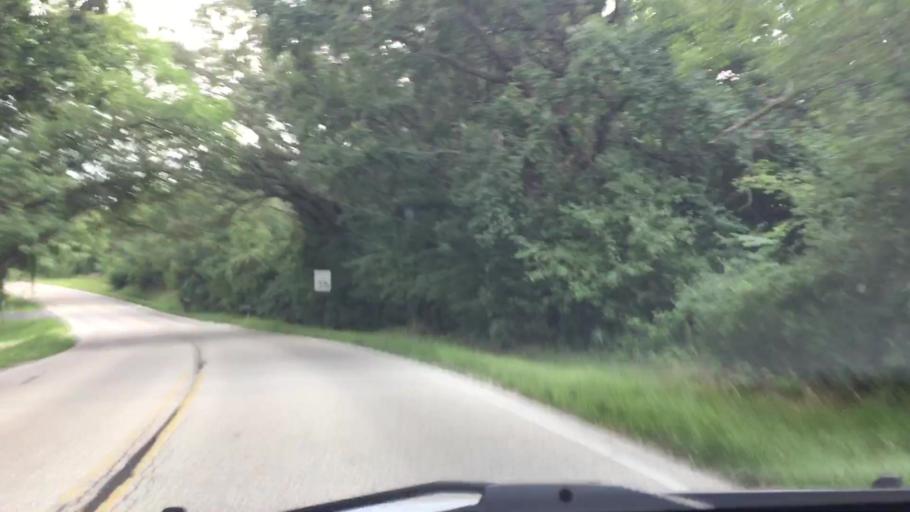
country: US
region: Wisconsin
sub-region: Waukesha County
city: Wales
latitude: 43.0282
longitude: -88.3654
